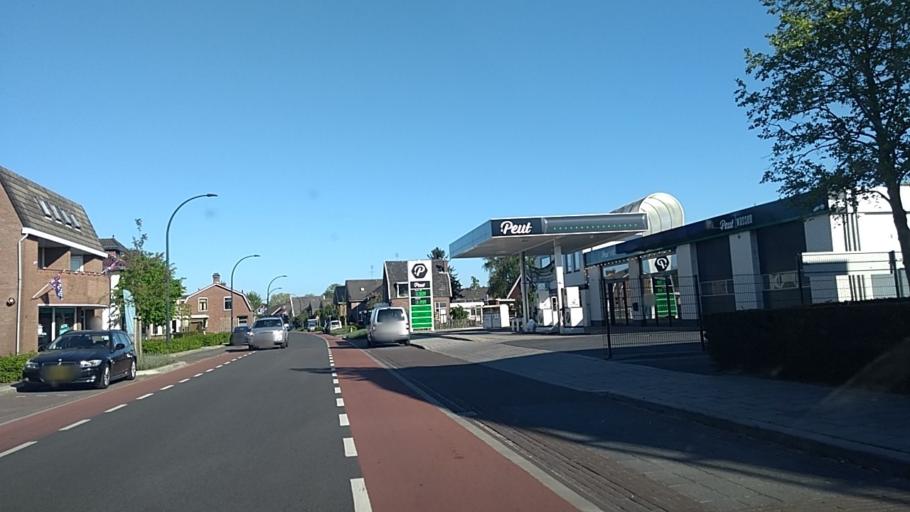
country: NL
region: Overijssel
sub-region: Gemeente Wierden
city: Wierden
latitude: 52.3597
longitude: 6.5835
